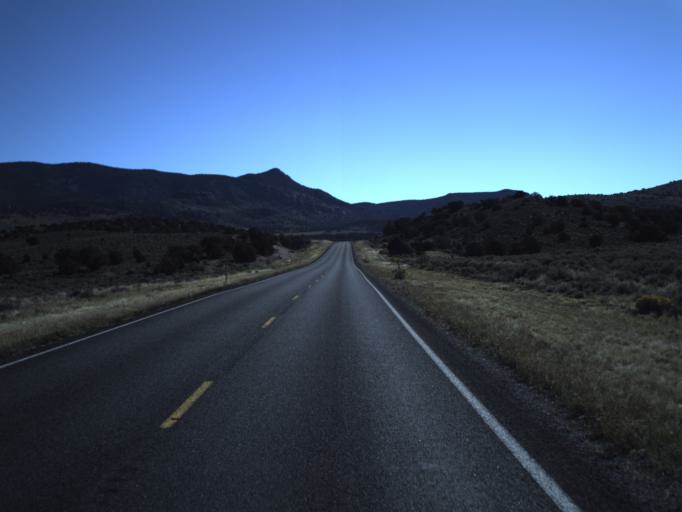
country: US
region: Utah
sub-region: Washington County
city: Enterprise
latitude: 37.6756
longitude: -113.5143
